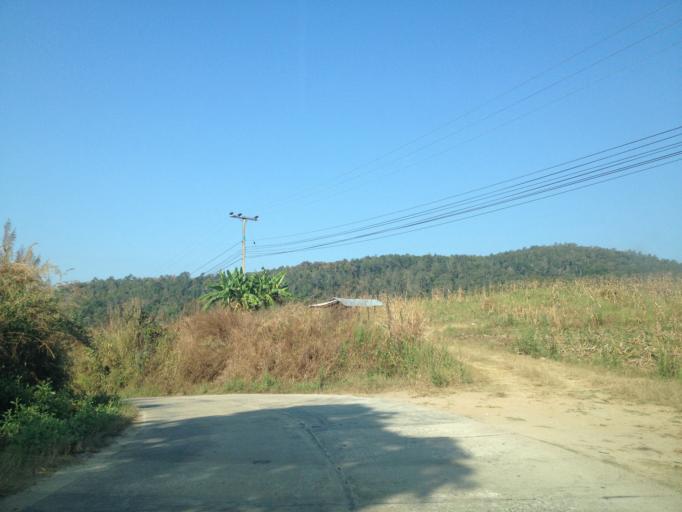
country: TH
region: Mae Hong Son
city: Ban Huai I Huak
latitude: 18.1517
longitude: 98.2155
